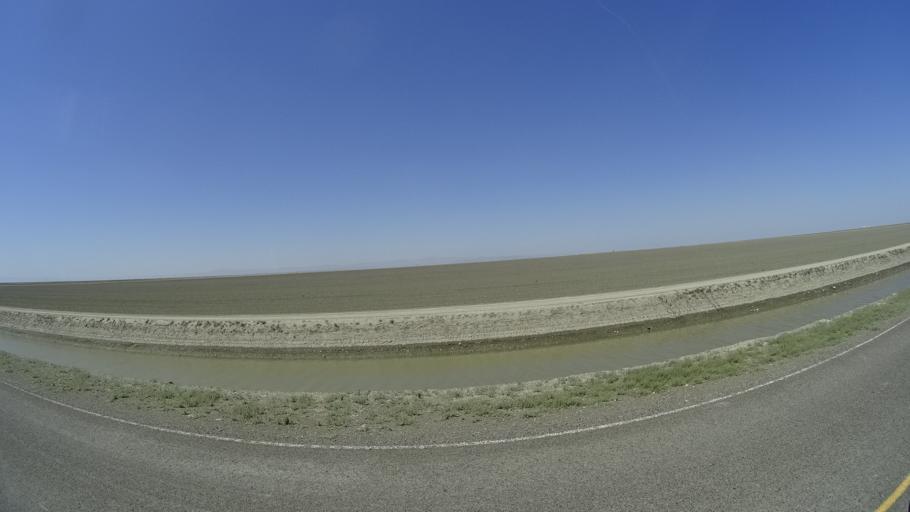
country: US
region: California
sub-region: Kings County
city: Corcoran
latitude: 35.9593
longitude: -119.6460
